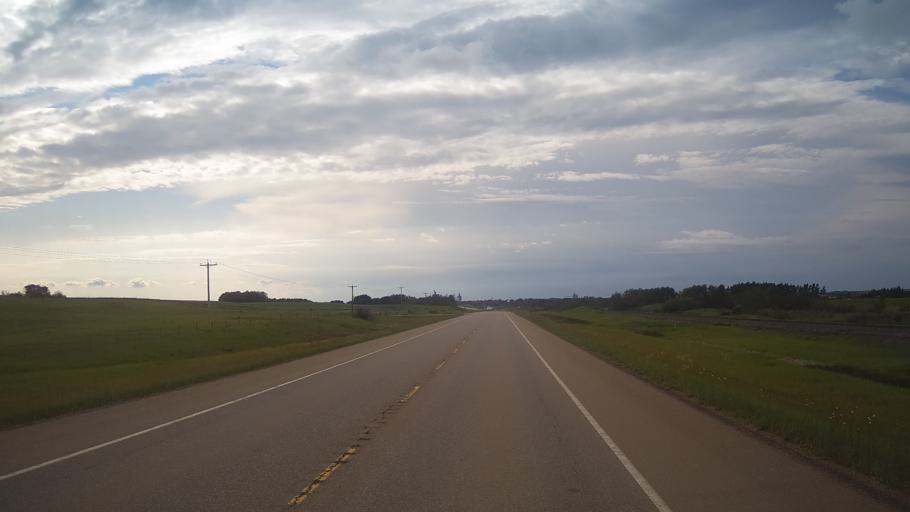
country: CA
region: Alberta
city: Viking
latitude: 53.0794
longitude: -111.7377
